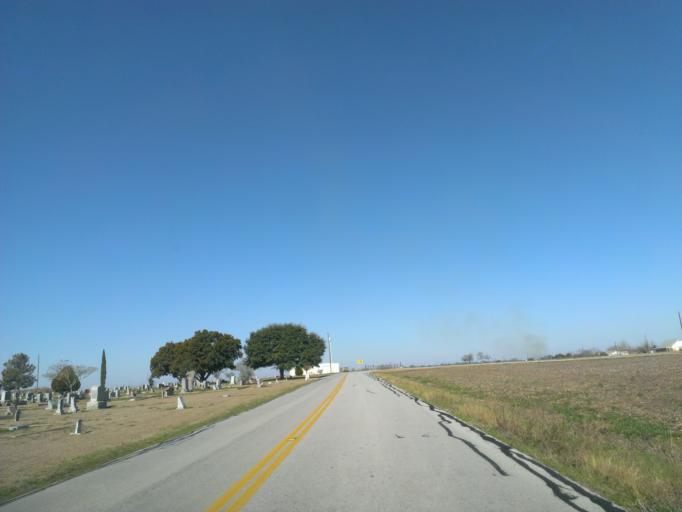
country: US
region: Texas
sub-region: Williamson County
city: Georgetown
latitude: 30.6614
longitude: -97.5822
